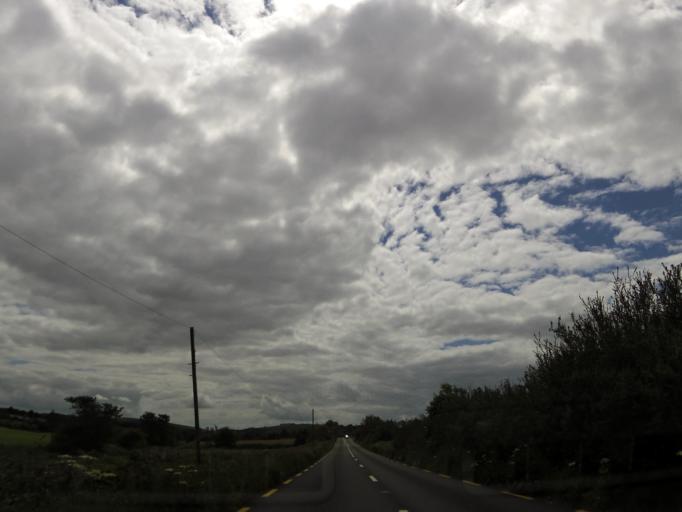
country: IE
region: Munster
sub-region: North Tipperary
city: Nenagh
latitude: 52.7874
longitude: -8.0356
